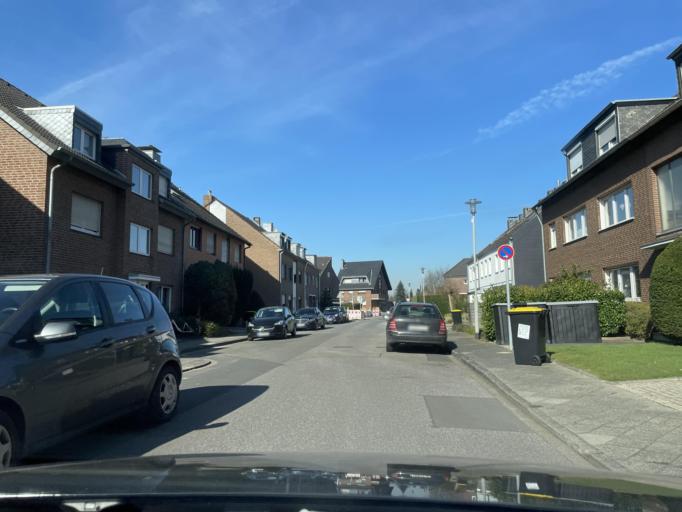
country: DE
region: North Rhine-Westphalia
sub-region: Regierungsbezirk Dusseldorf
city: Monchengladbach
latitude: 51.1993
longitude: 6.3942
